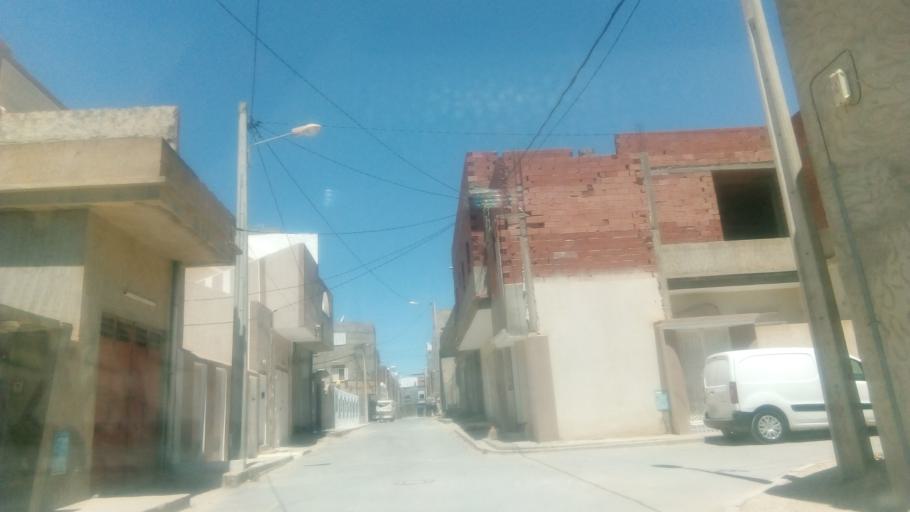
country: TN
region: Al Qayrawan
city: Kairouan
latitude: 35.6664
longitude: 10.0858
